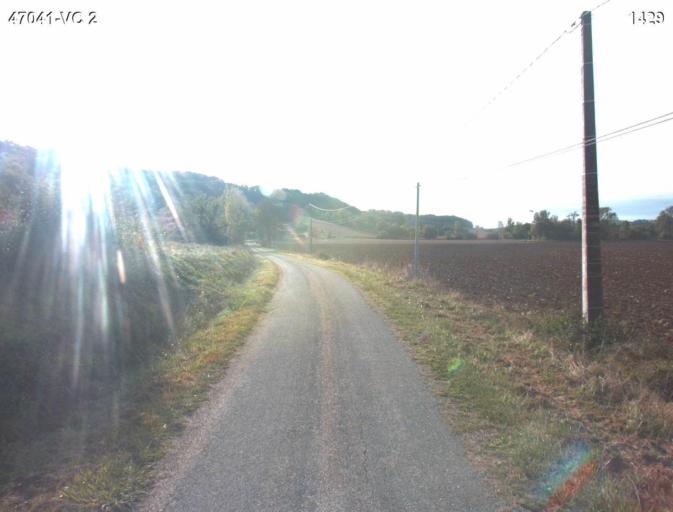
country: FR
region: Aquitaine
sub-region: Departement du Lot-et-Garonne
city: Port-Sainte-Marie
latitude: 44.1904
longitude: 0.4159
